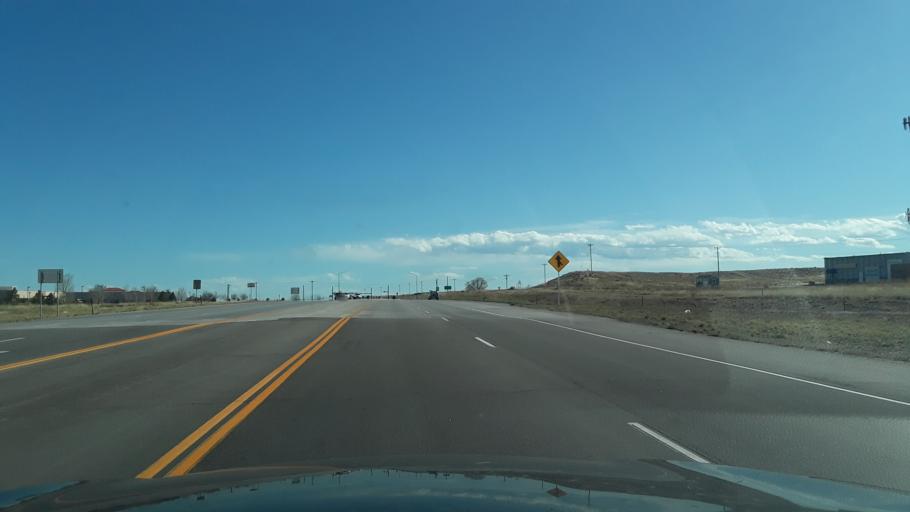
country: US
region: Colorado
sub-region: Pueblo County
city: Pueblo West
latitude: 38.3135
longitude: -104.6615
